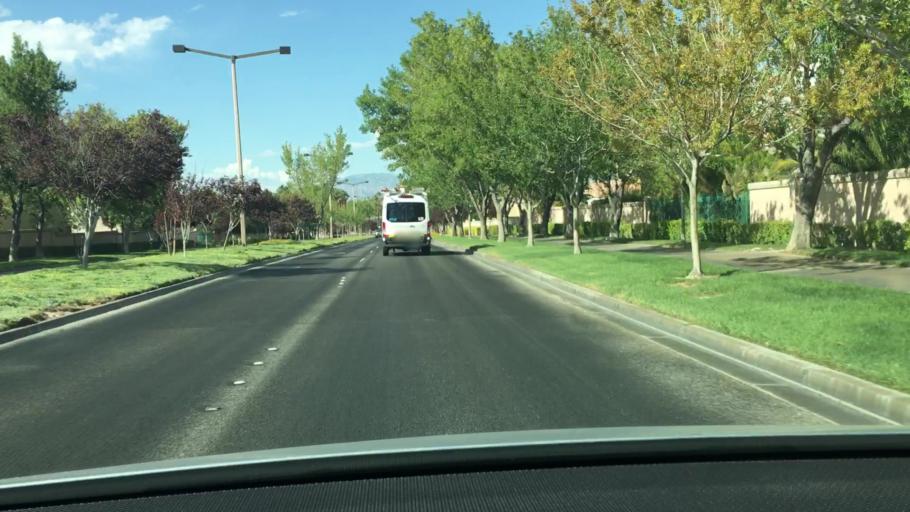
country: US
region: Nevada
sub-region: Clark County
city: Summerlin South
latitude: 36.2027
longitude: -115.3003
